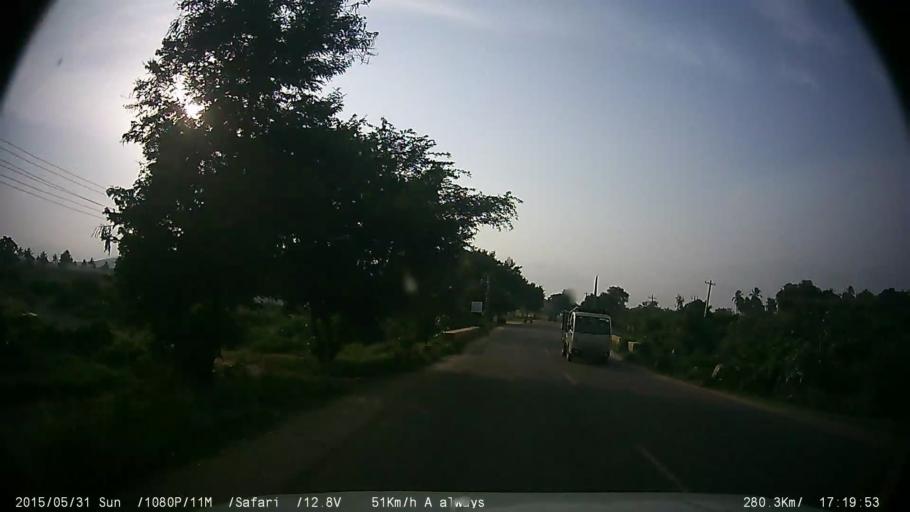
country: IN
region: Karnataka
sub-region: Chamrajnagar
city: Gundlupet
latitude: 11.8186
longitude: 76.6835
